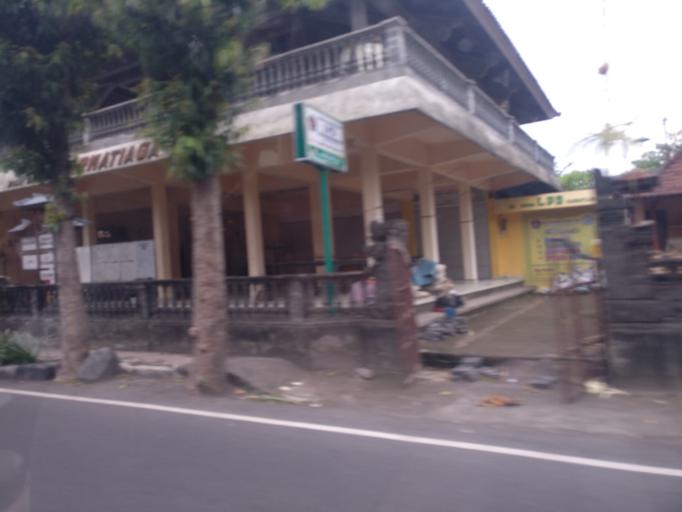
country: ID
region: Bali
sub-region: Kabupaten Gianyar
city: Ubud
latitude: -8.5575
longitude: 115.3020
